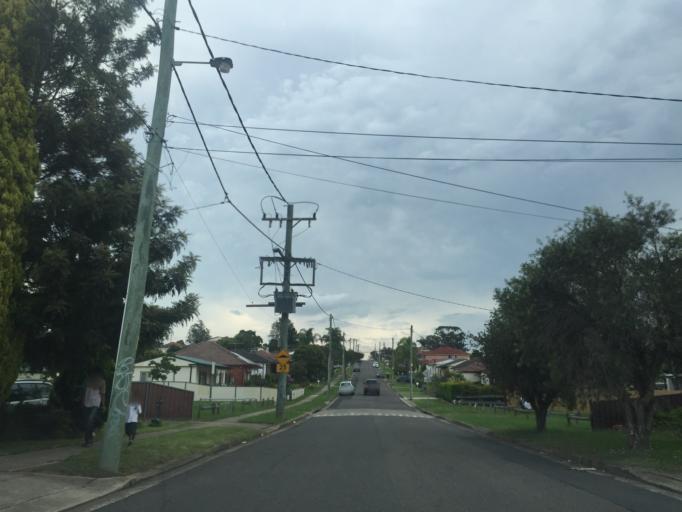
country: AU
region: New South Wales
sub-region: Blacktown
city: Blacktown
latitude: -33.7833
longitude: 150.8994
